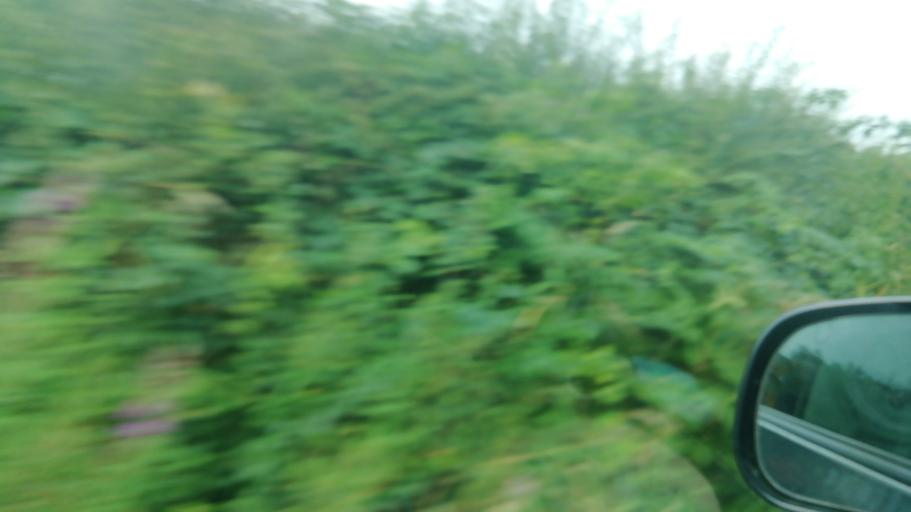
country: IE
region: Munster
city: Fethard
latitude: 52.5676
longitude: -7.5792
